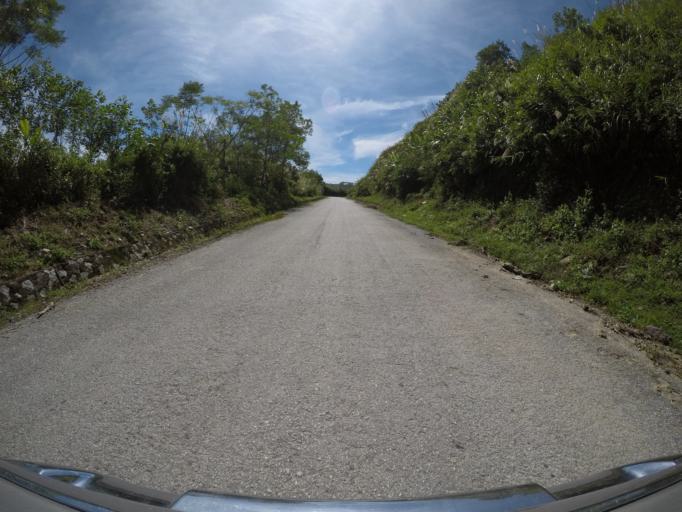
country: VN
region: Quang Nam
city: Thanh My
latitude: 15.6592
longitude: 107.6781
